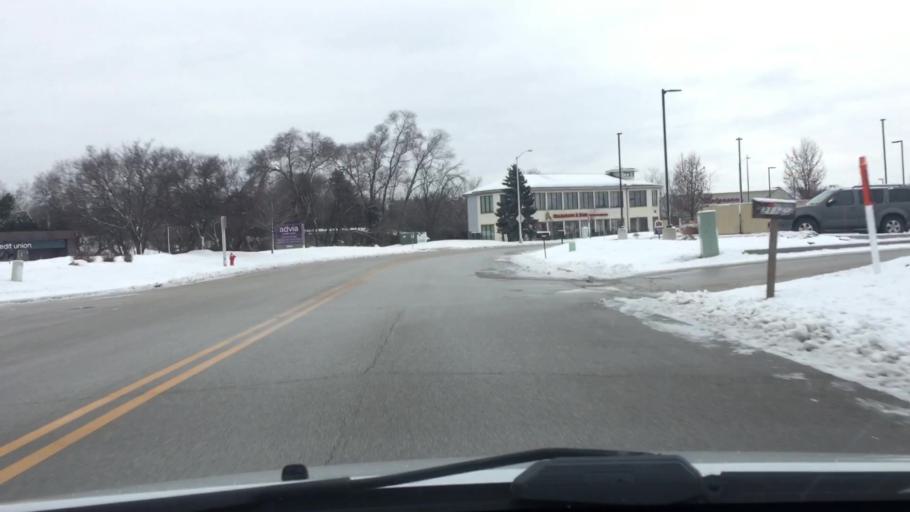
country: US
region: Wisconsin
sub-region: Waukesha County
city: Waukesha
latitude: 43.0316
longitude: -88.1757
